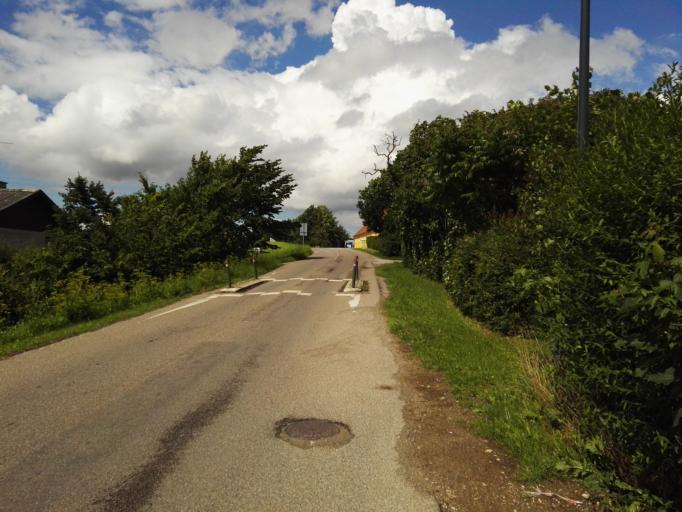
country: DK
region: Capital Region
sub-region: Egedal Kommune
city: Vekso
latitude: 55.7751
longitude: 12.2342
